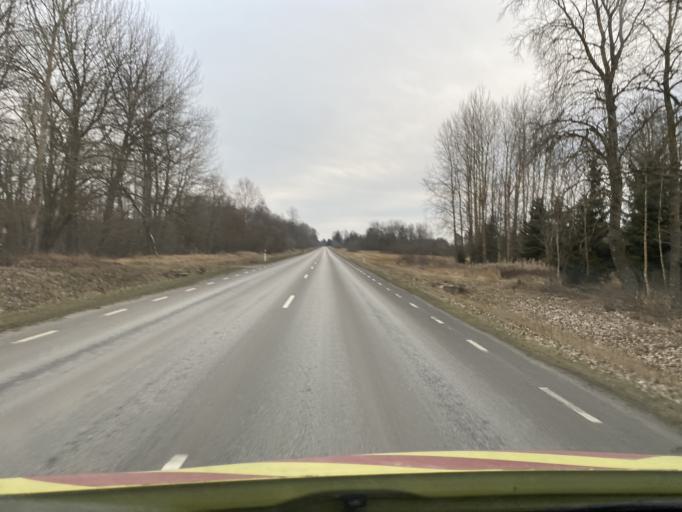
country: EE
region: Laeaene
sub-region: Ridala Parish
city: Uuemoisa
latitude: 58.8960
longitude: 23.5887
